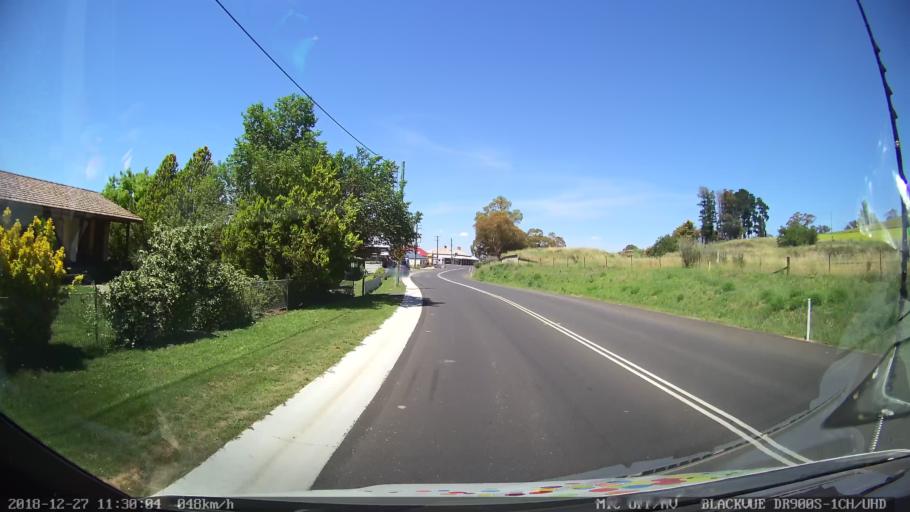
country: AU
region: New South Wales
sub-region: Bathurst Regional
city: Perthville
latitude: -33.4851
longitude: 149.5477
